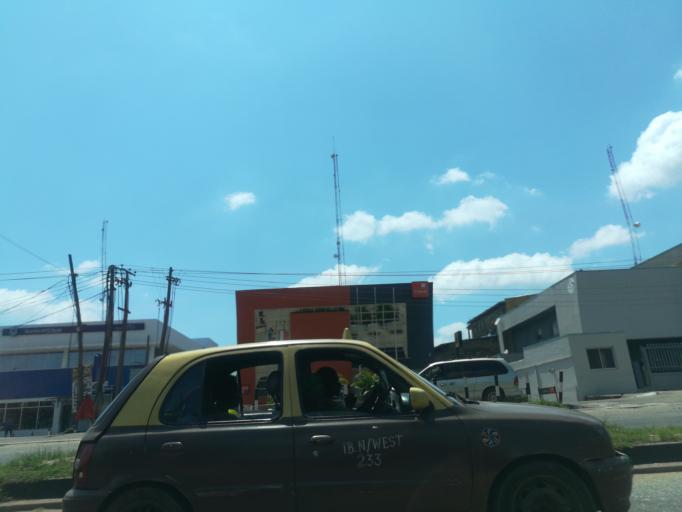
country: NG
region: Oyo
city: Ibadan
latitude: 7.3612
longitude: 3.8681
